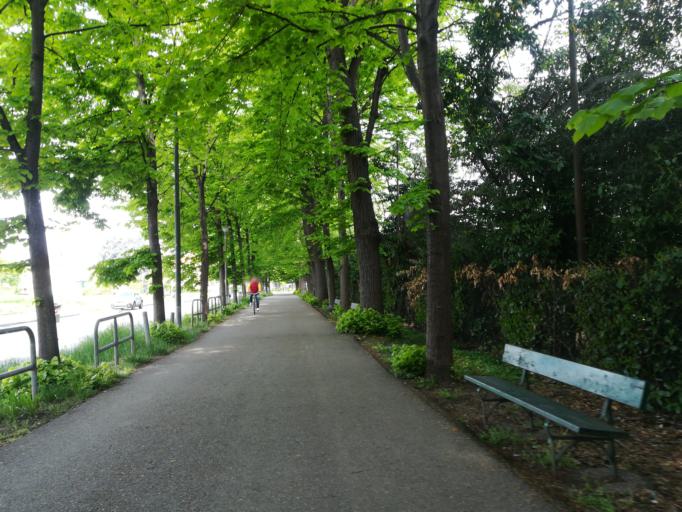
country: IT
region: Piedmont
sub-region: Provincia di Torino
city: Nichelino
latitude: 45.0169
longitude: 7.6255
